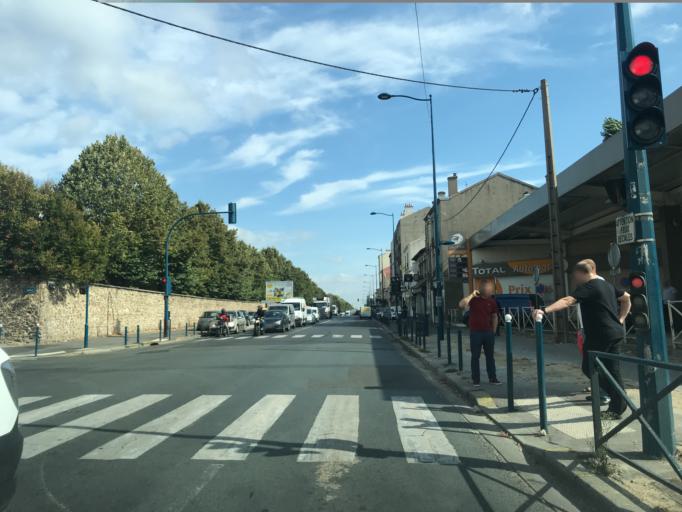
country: FR
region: Ile-de-France
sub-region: Departement de Seine-Saint-Denis
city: Pantin
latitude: 48.9003
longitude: 2.4106
